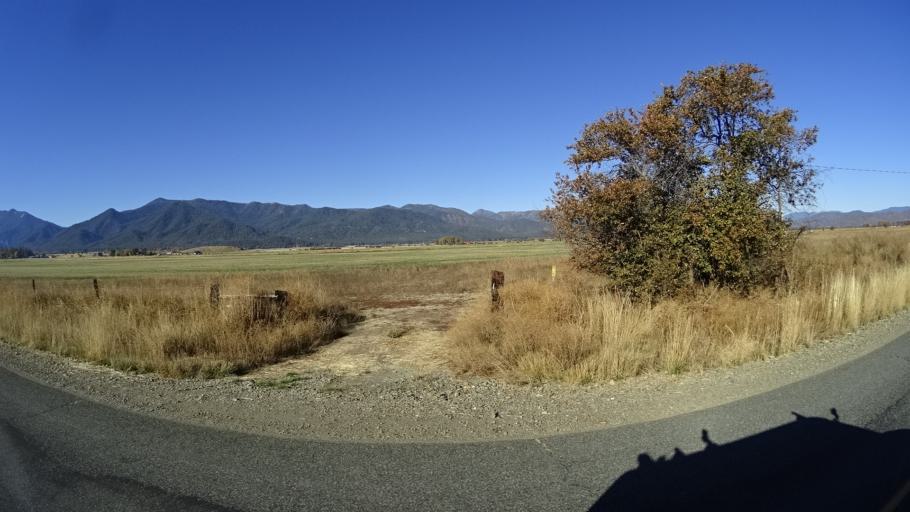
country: US
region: California
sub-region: Siskiyou County
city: Yreka
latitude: 41.4961
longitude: -122.8592
